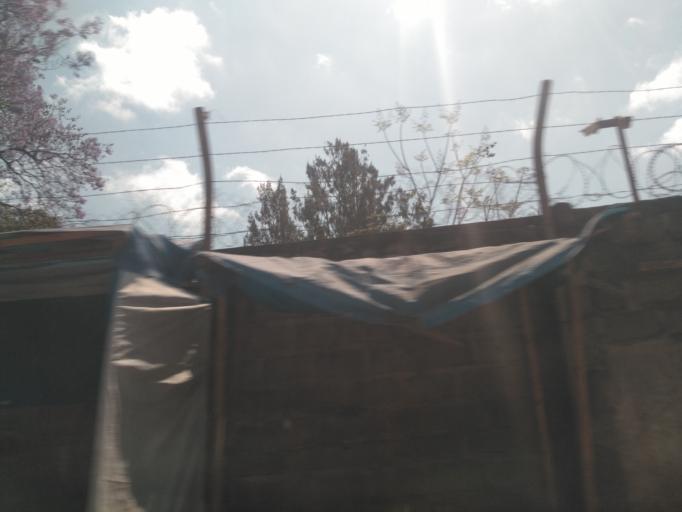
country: TZ
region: Arusha
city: Arusha
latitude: -3.3722
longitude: 36.6818
